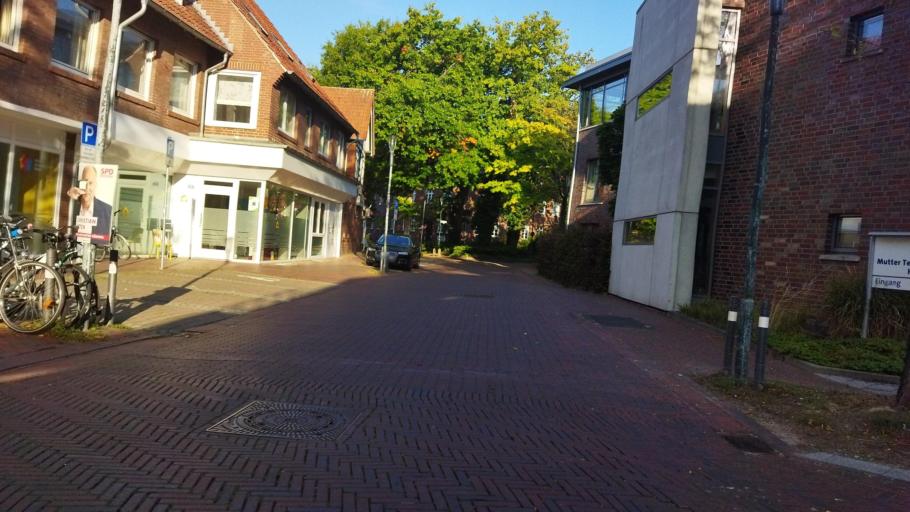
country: DE
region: Lower Saxony
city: Lingen
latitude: 52.5240
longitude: 7.3139
